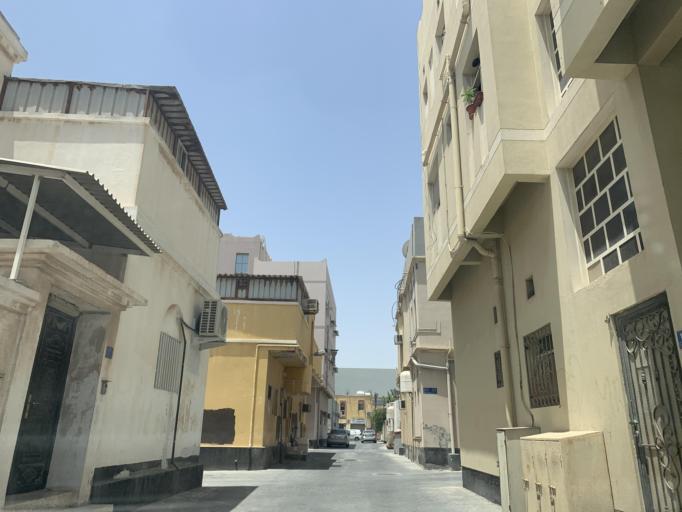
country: BH
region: Northern
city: Sitrah
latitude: 26.1604
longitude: 50.6228
